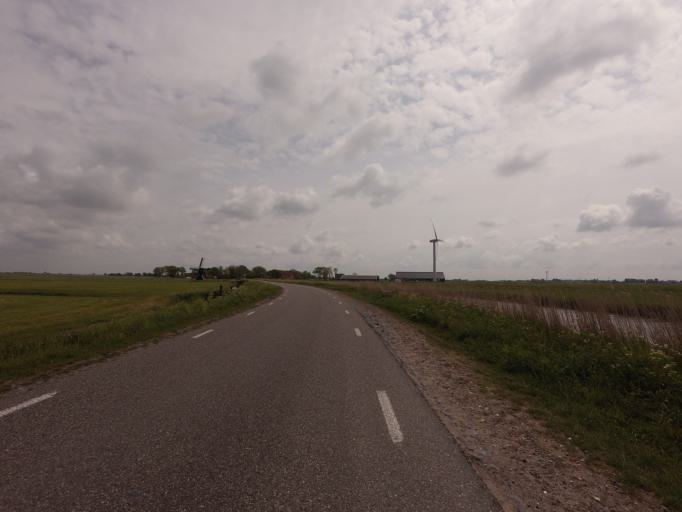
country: NL
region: Friesland
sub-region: Sudwest Fryslan
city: Bolsward
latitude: 53.1004
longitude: 5.5165
